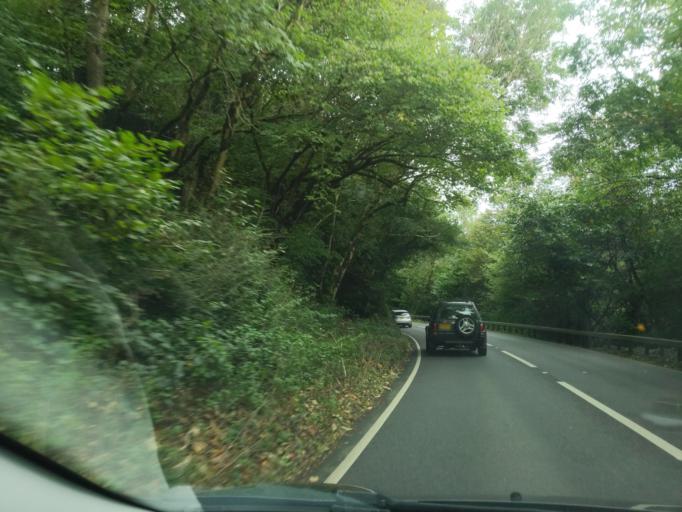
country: GB
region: England
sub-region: Cornwall
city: Wadebridge
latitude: 50.5070
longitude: -4.7816
